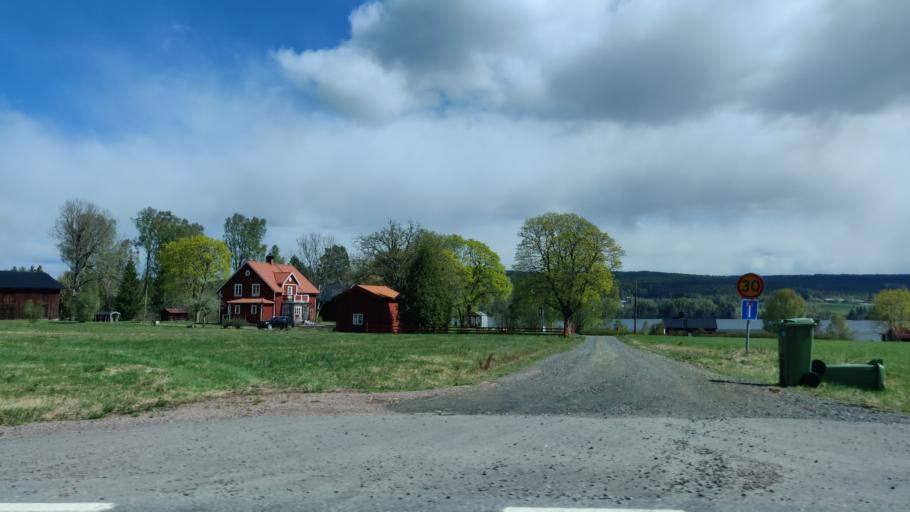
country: SE
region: Vaermland
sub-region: Munkfors Kommun
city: Munkfors
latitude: 59.8512
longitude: 13.7100
